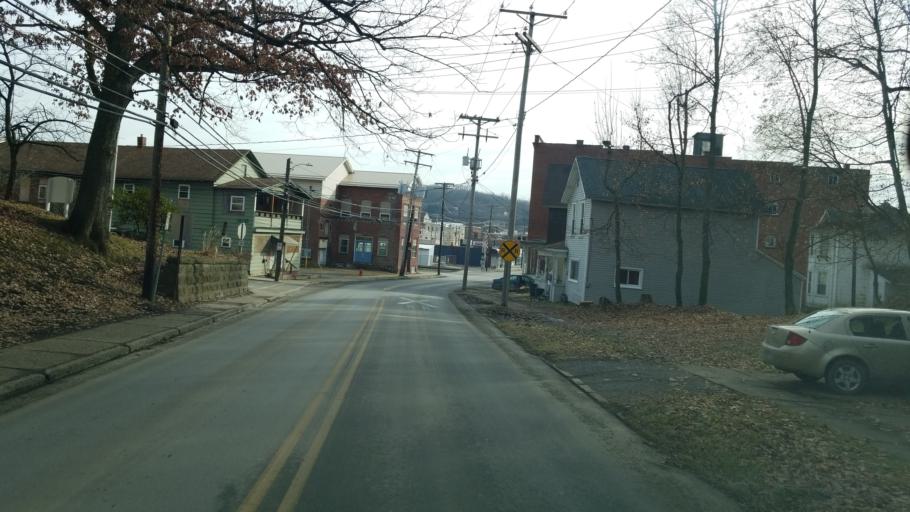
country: US
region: Pennsylvania
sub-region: Jefferson County
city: Punxsutawney
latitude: 40.9470
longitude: -78.9730
